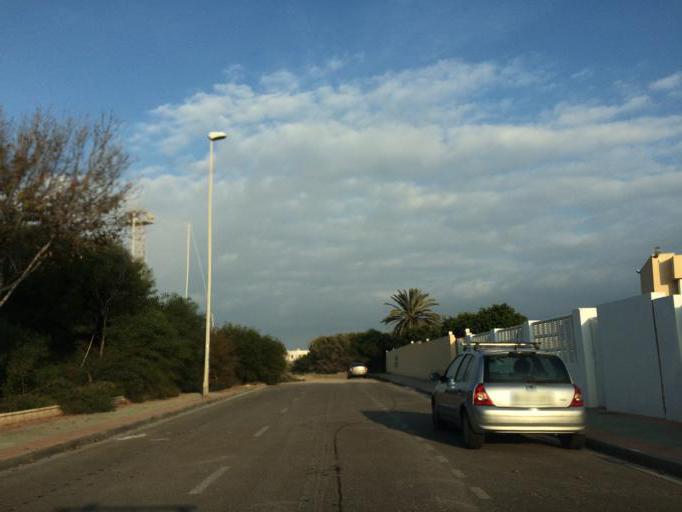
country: ES
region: Andalusia
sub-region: Provincia de Almeria
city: Almeria
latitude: 36.8253
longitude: -2.4356
